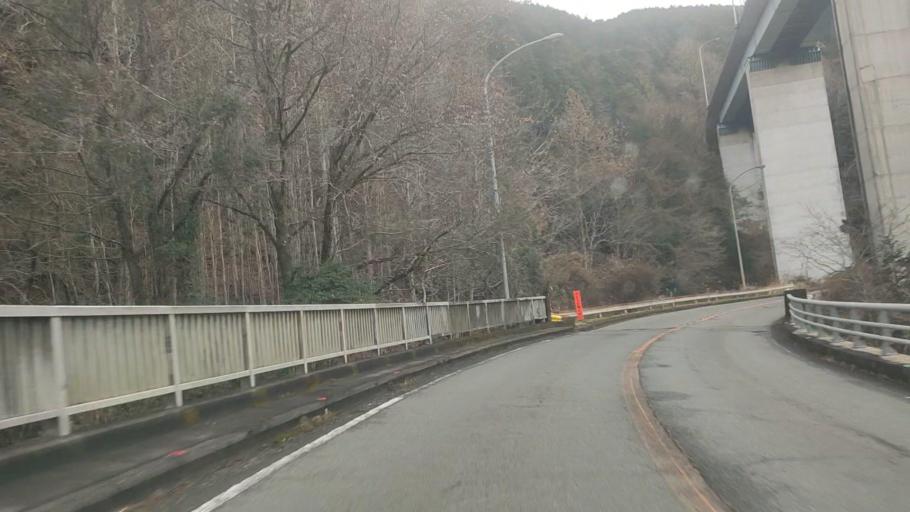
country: JP
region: Kumamoto
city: Hitoyoshi
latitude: 32.1216
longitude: 130.8127
